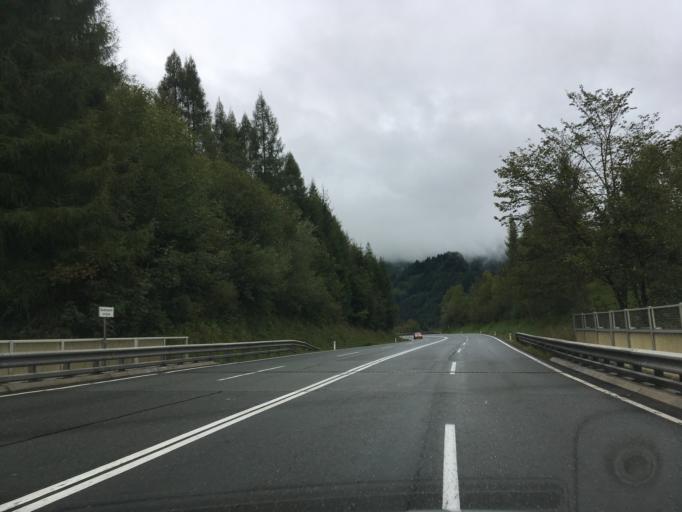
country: AT
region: Salzburg
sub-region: Politischer Bezirk Zell am See
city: Lend
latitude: 47.2976
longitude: 13.0420
